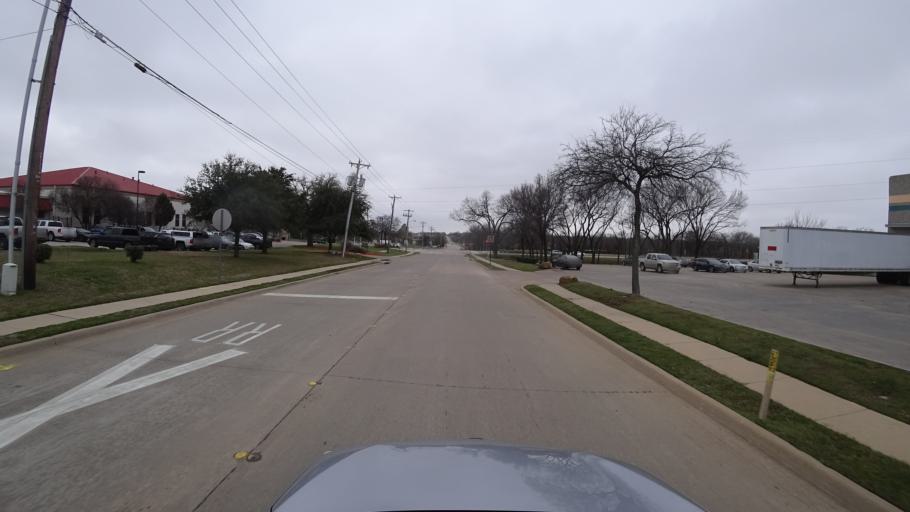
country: US
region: Texas
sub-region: Denton County
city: Lewisville
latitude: 33.0579
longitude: -96.9927
